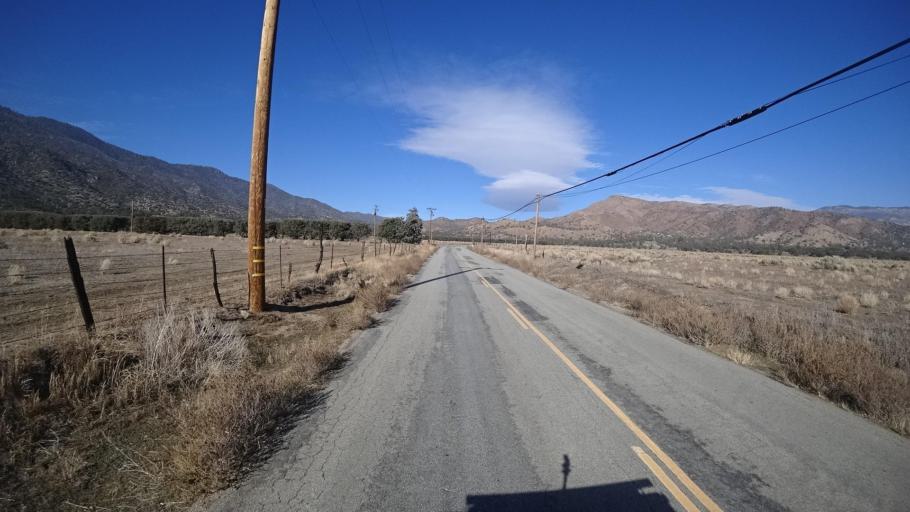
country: US
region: California
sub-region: Kern County
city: Bodfish
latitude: 35.4235
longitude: -118.5369
